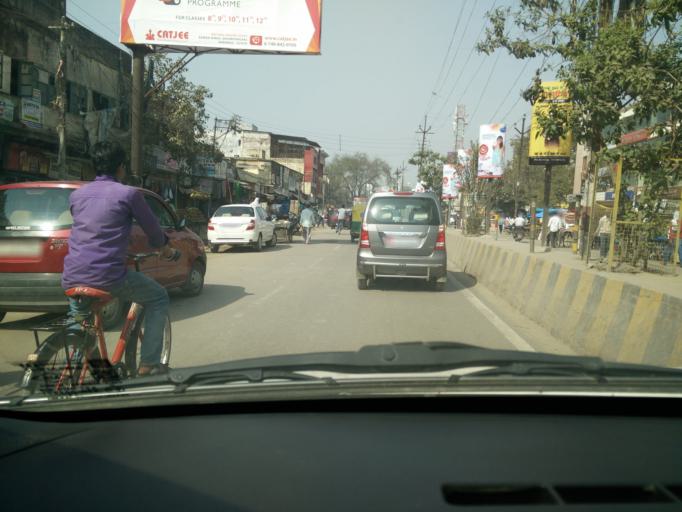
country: IN
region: Uttar Pradesh
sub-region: Varanasi
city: Ramnagar
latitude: 25.2809
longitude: 83.0030
